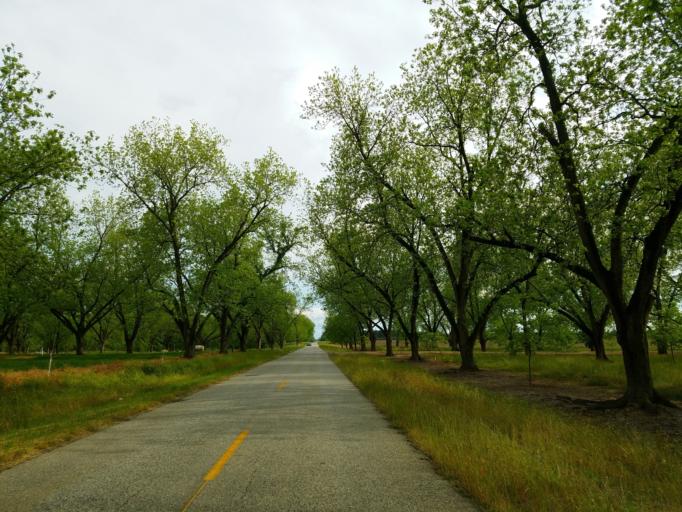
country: US
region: Georgia
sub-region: Dooly County
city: Vienna
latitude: 32.1587
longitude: -83.7607
